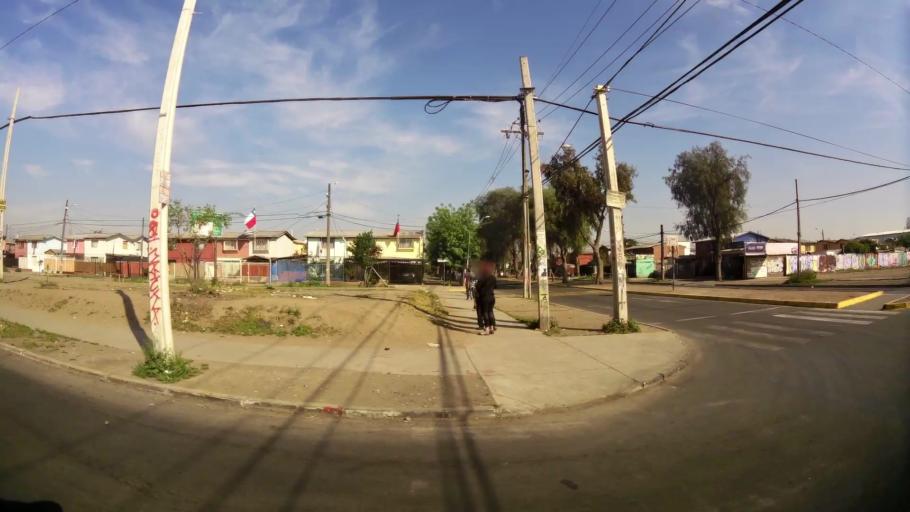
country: CL
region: Santiago Metropolitan
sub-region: Provincia de Santiago
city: Lo Prado
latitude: -33.4559
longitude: -70.7511
